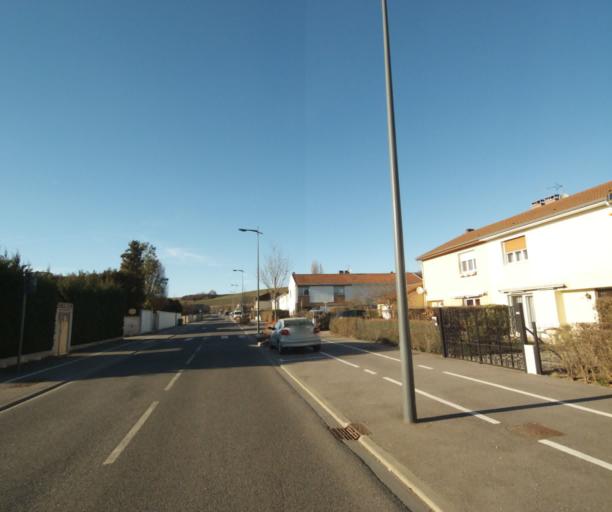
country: FR
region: Lorraine
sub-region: Departement de Meurthe-et-Moselle
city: Seichamps
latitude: 48.7123
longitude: 6.2524
